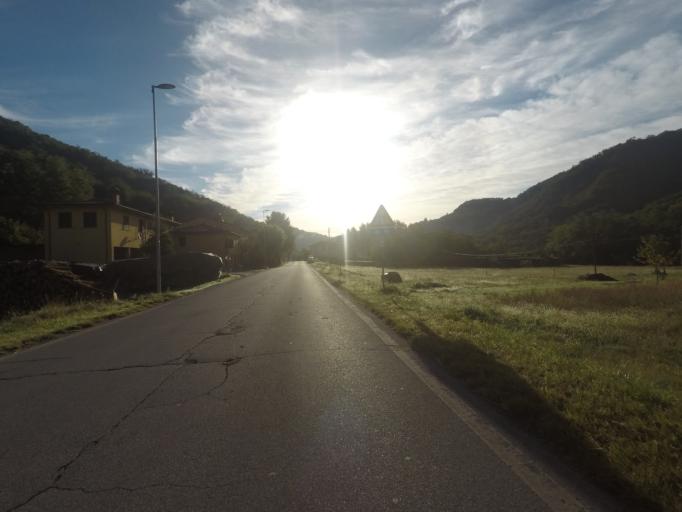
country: IT
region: Tuscany
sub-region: Provincia di Lucca
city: Pescaglia
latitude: 43.9523
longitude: 10.4361
